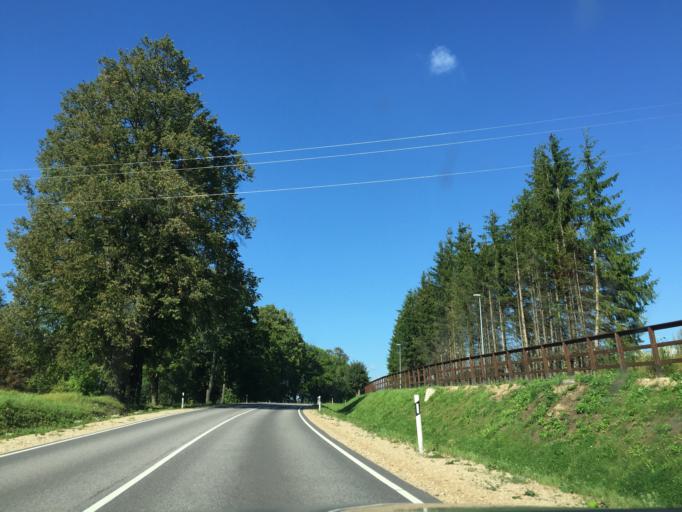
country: LV
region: Limbazu Rajons
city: Limbazi
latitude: 57.4905
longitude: 24.7089
